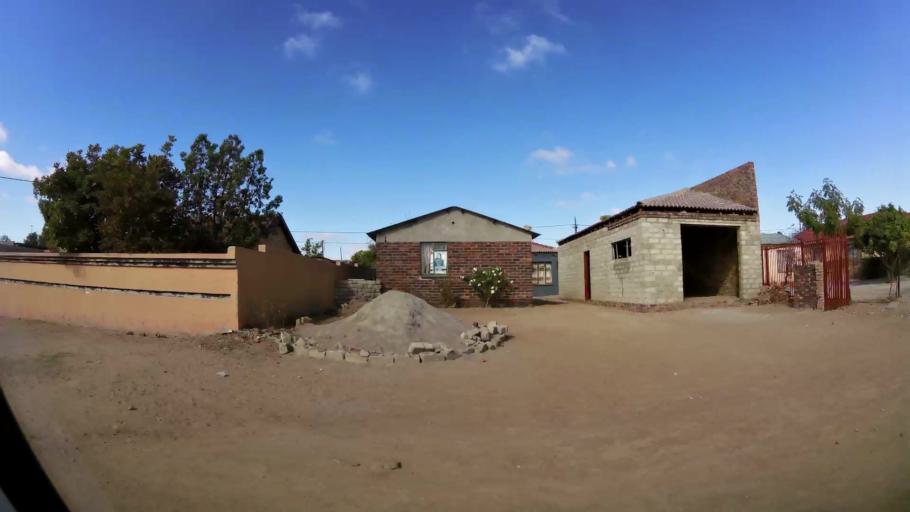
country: ZA
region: Limpopo
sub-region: Capricorn District Municipality
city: Polokwane
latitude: -23.8587
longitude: 29.3662
